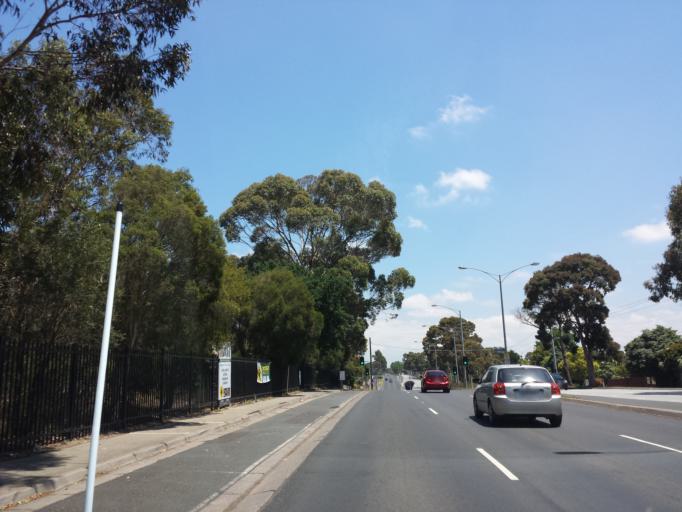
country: AU
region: Victoria
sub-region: Knox
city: Bayswater
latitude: -37.8422
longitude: 145.2595
